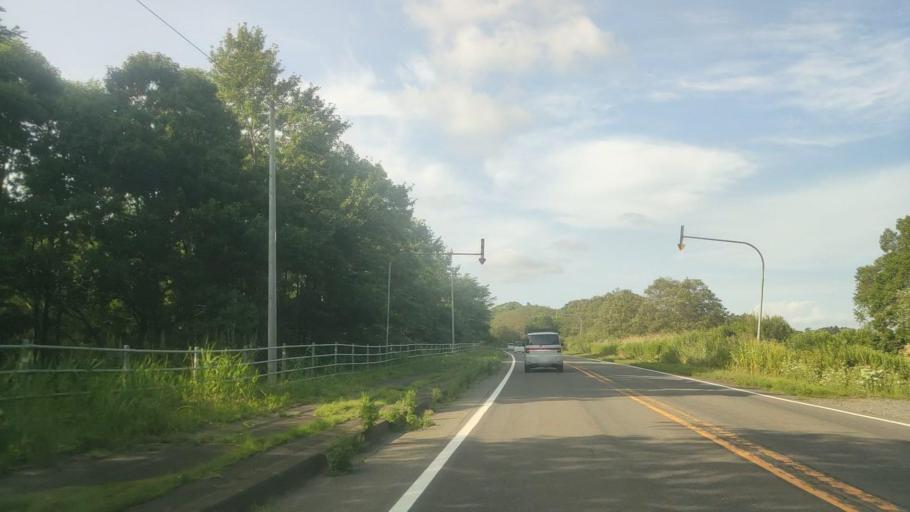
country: JP
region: Hokkaido
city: Chitose
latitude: 42.8613
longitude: 141.8223
